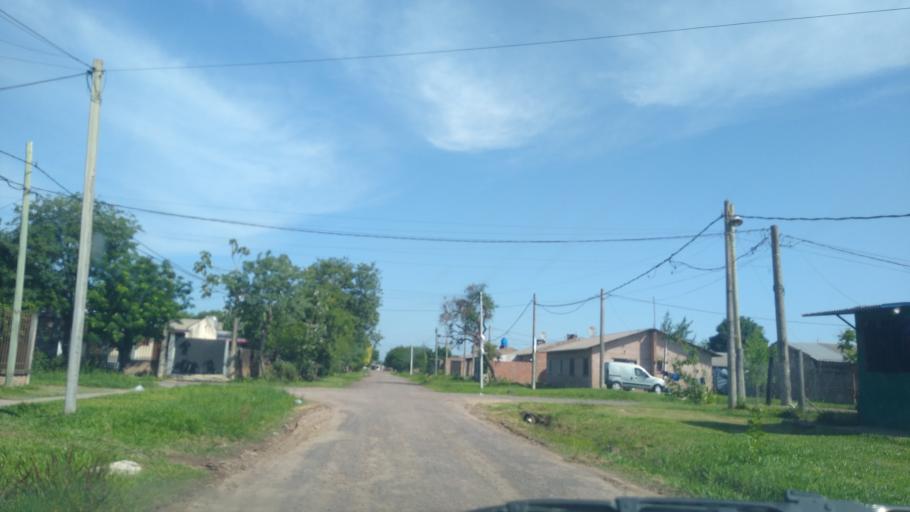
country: AR
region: Chaco
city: Puerto Vilelas
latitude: -27.4986
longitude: -58.9594
